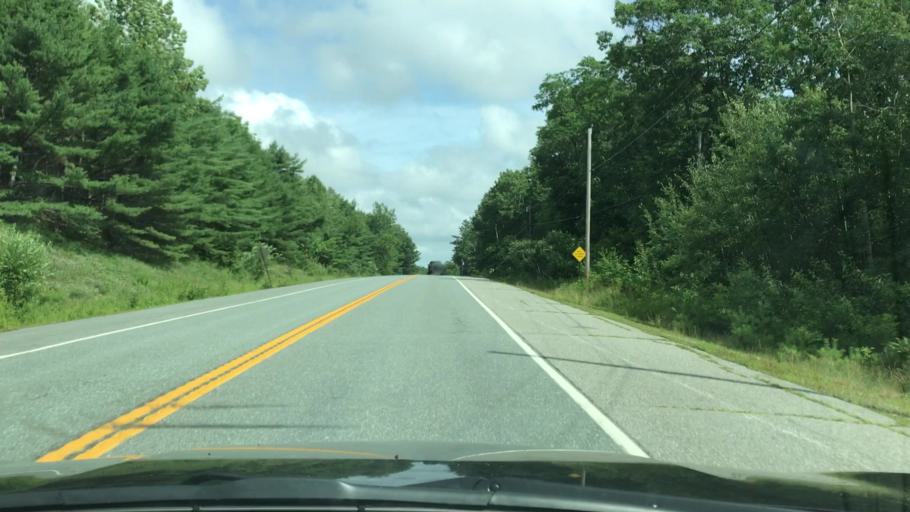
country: US
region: Maine
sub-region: Hancock County
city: Orland
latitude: 44.5667
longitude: -68.6720
